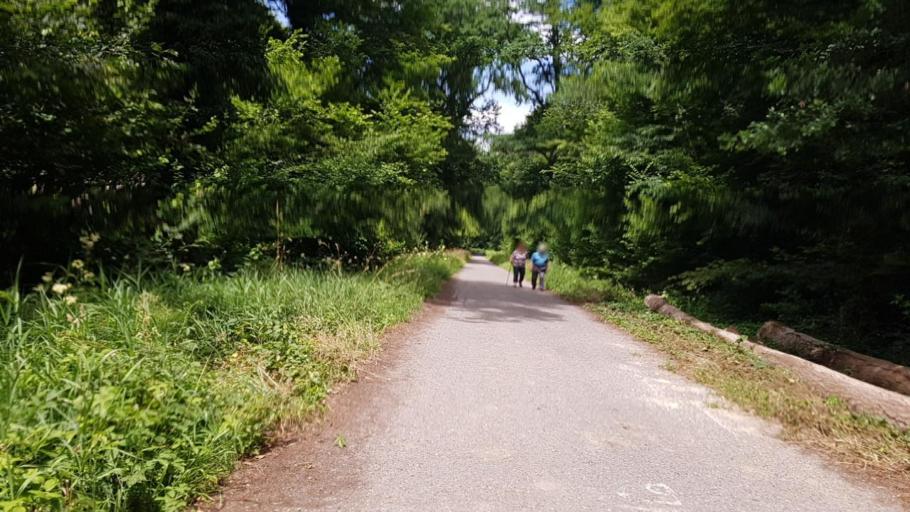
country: FR
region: Picardie
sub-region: Departement de l'Oise
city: Montmacq
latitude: 49.4749
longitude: 2.9179
